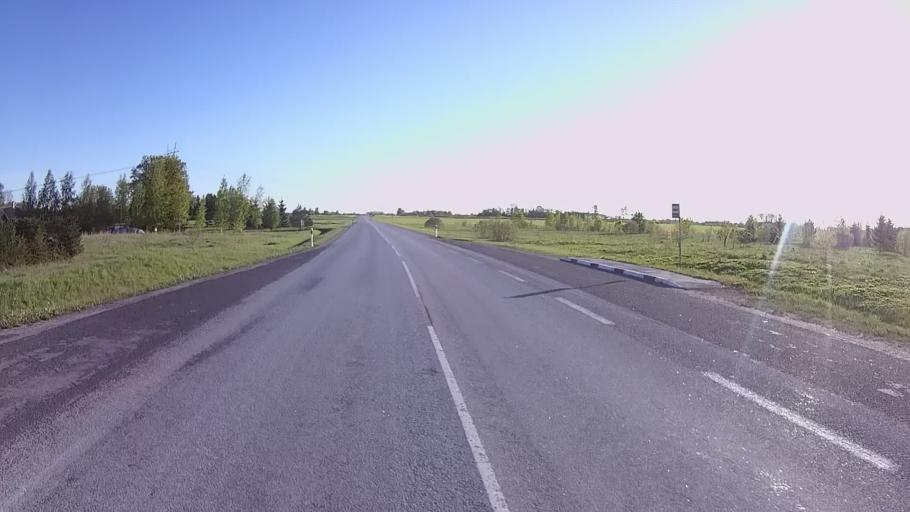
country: EE
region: Viljandimaa
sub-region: Viiratsi vald
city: Viiratsi
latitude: 58.3949
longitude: 25.6363
